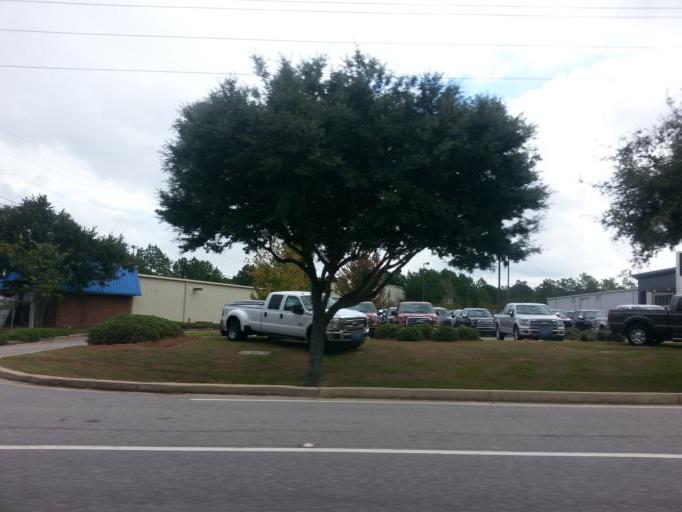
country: US
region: Alabama
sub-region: Baldwin County
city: Daphne
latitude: 30.6213
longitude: -87.9064
